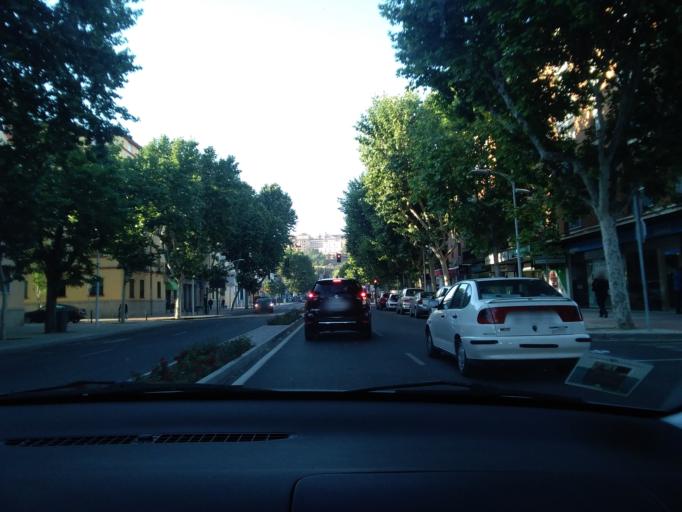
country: ES
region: Castille-La Mancha
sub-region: Province of Toledo
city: Toledo
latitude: 39.8670
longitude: -4.0291
